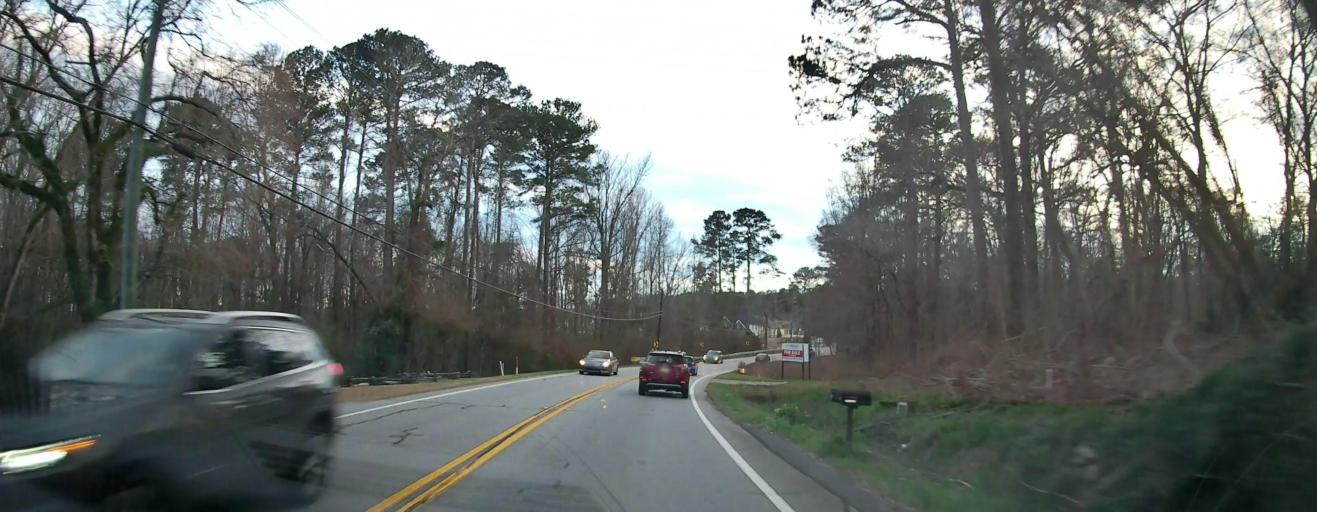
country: US
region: Alabama
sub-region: Russell County
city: Phenix City
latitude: 32.5785
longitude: -84.9118
